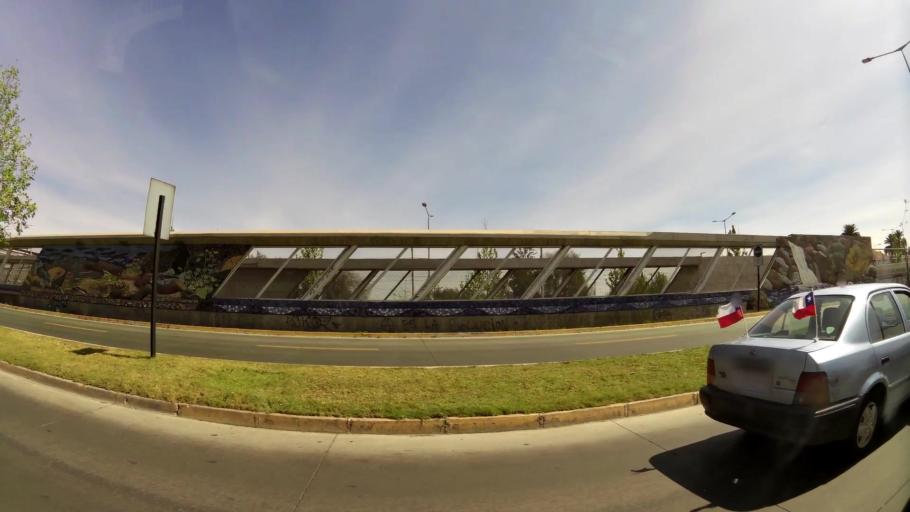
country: CL
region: Santiago Metropolitan
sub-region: Provincia de Cordillera
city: Puente Alto
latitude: -33.5967
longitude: -70.5782
